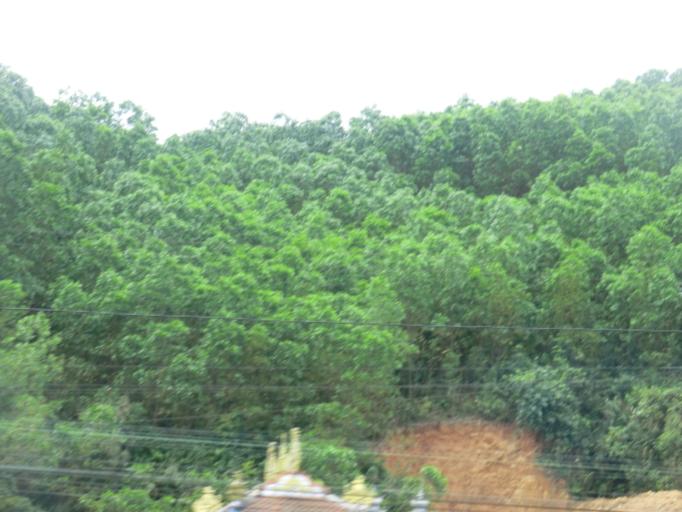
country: VN
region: Thua Thien-Hue
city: Phu Loc
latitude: 16.3044
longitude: 107.7977
